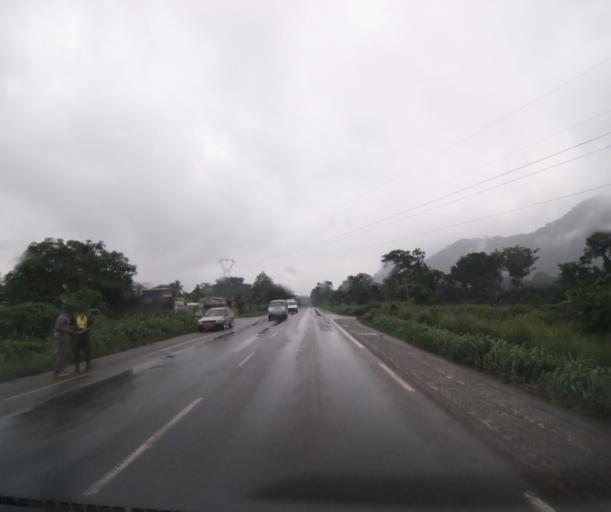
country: CM
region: Centre
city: Eseka
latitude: 3.8917
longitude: 10.7724
